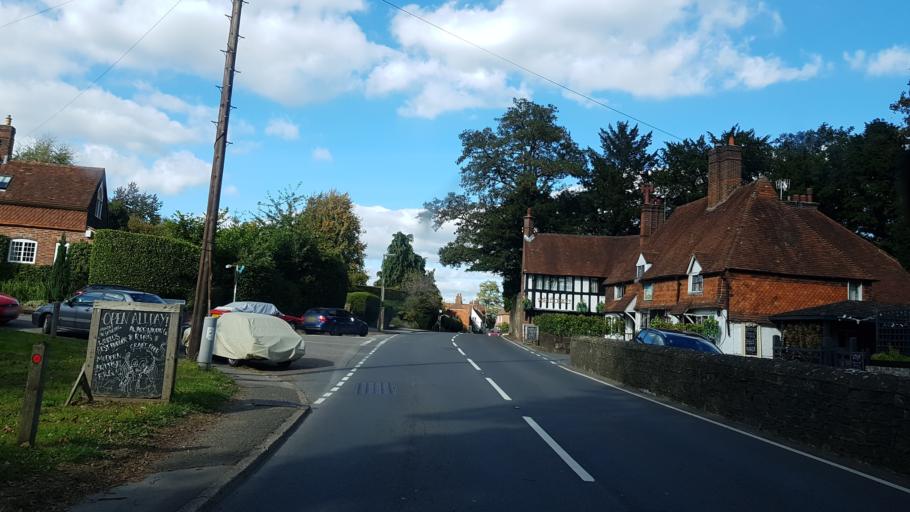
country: GB
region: England
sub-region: Surrey
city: Milford
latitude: 51.1482
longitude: -0.6469
